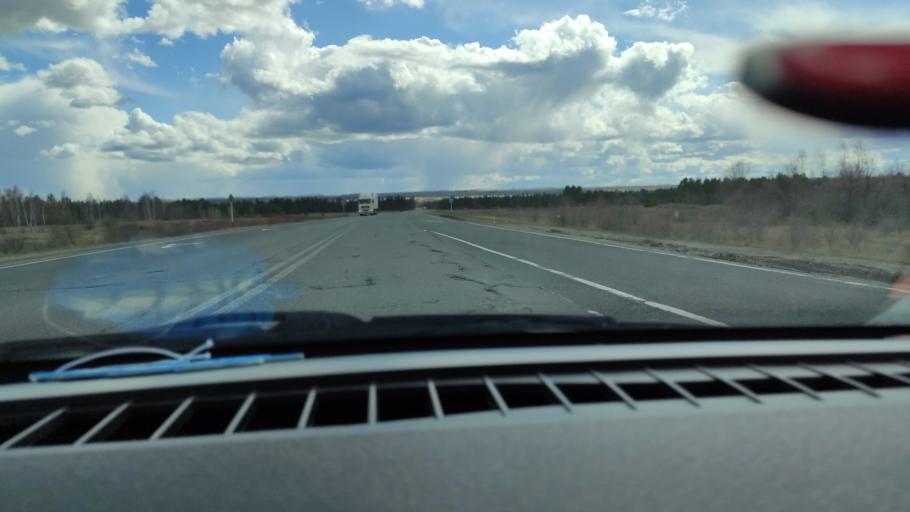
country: RU
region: Samara
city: Varlamovo
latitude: 53.1511
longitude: 48.2843
